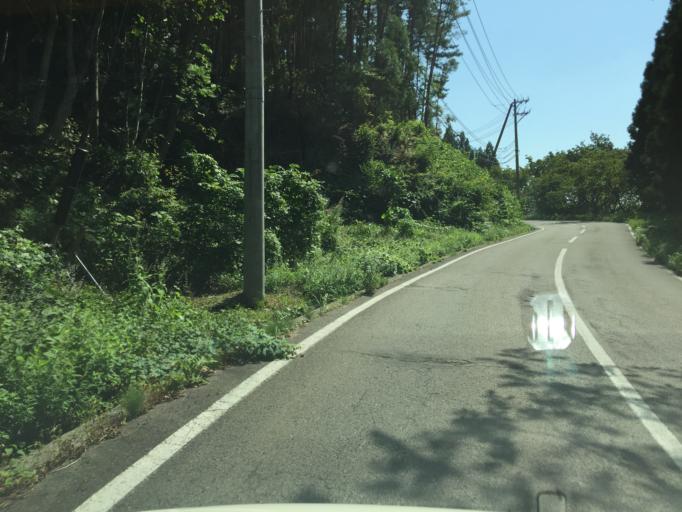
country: JP
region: Fukushima
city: Inawashiro
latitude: 37.5769
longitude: 140.0223
